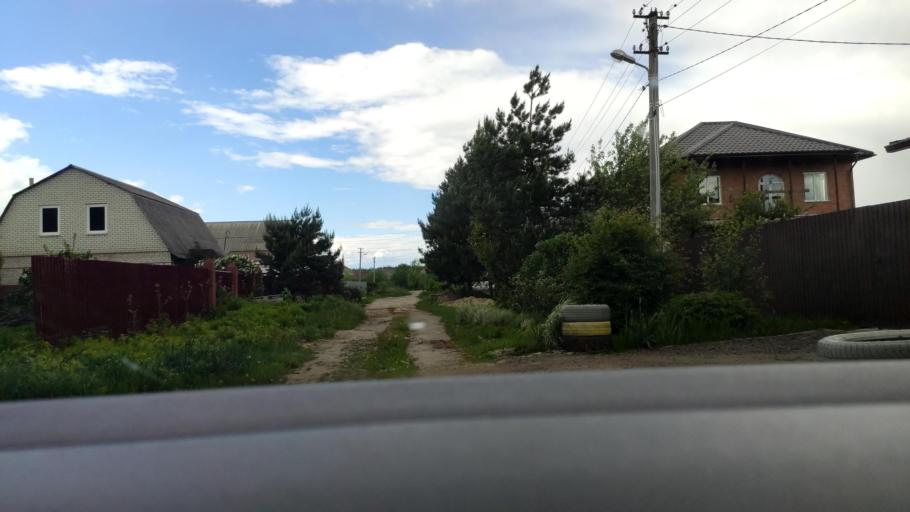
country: RU
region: Voronezj
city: Somovo
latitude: 51.6815
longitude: 39.3110
